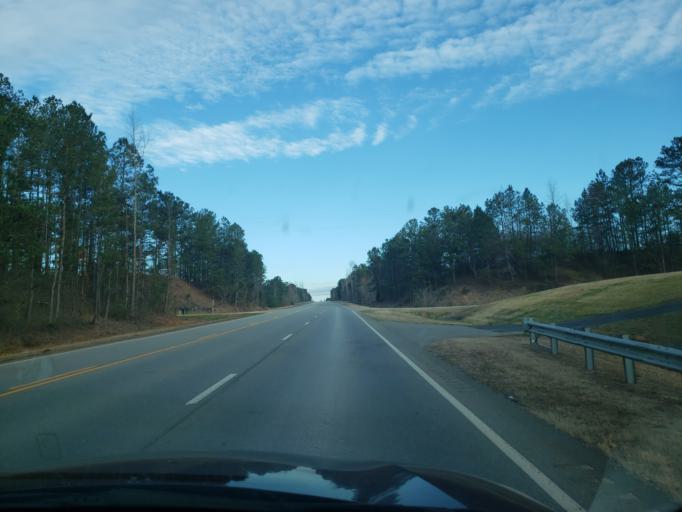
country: US
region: Alabama
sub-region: Randolph County
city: Wedowee
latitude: 33.4380
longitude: -85.5607
